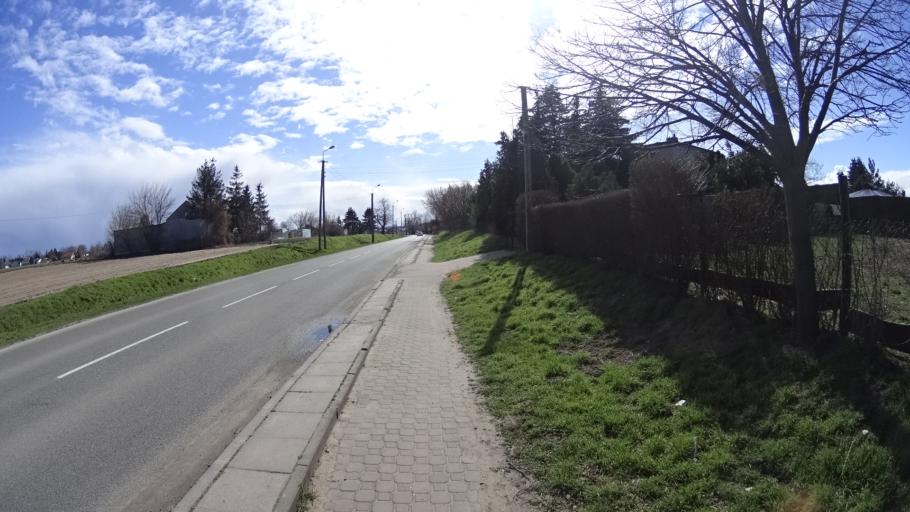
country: PL
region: Masovian Voivodeship
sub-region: Powiat warszawski zachodni
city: Jozefow
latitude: 52.2067
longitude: 20.6971
